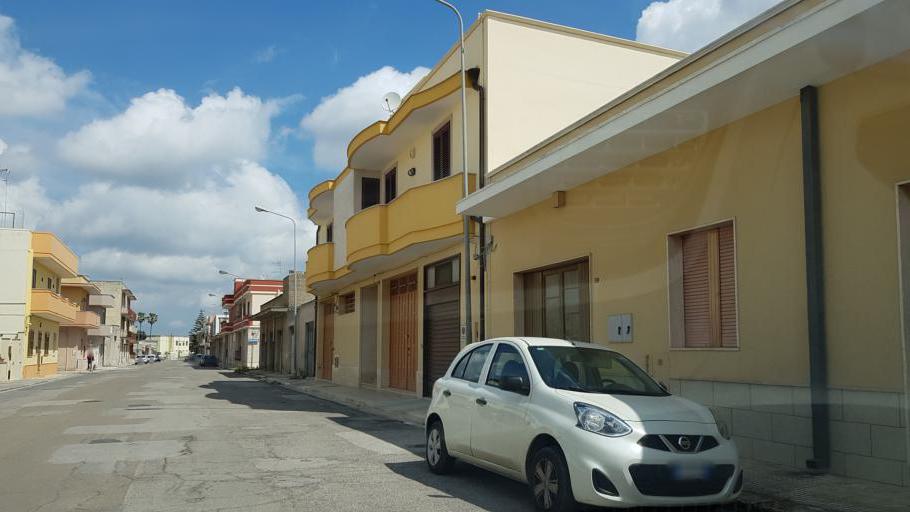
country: IT
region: Apulia
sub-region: Provincia di Brindisi
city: Mesagne
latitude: 40.5543
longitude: 17.8173
